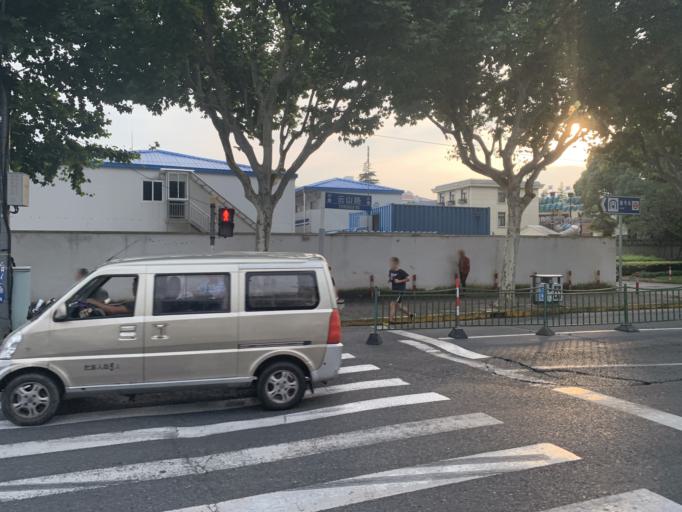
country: CN
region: Shanghai Shi
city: Huamu
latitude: 31.2445
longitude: 121.5727
